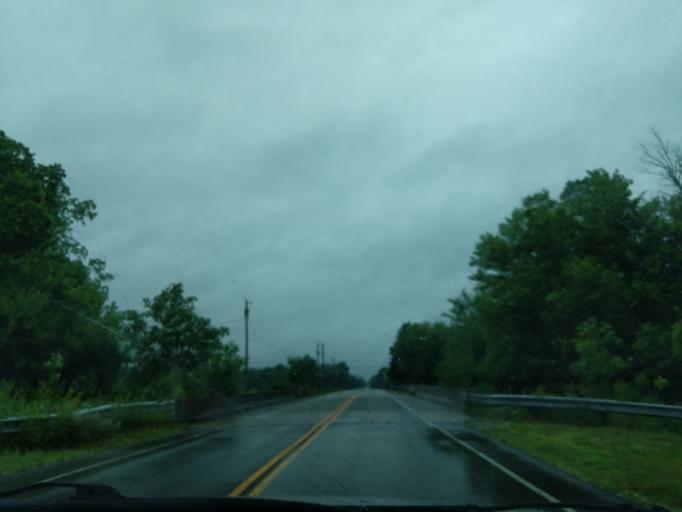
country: US
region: Indiana
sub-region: Madison County
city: Lapel
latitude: 40.0671
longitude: -85.8736
